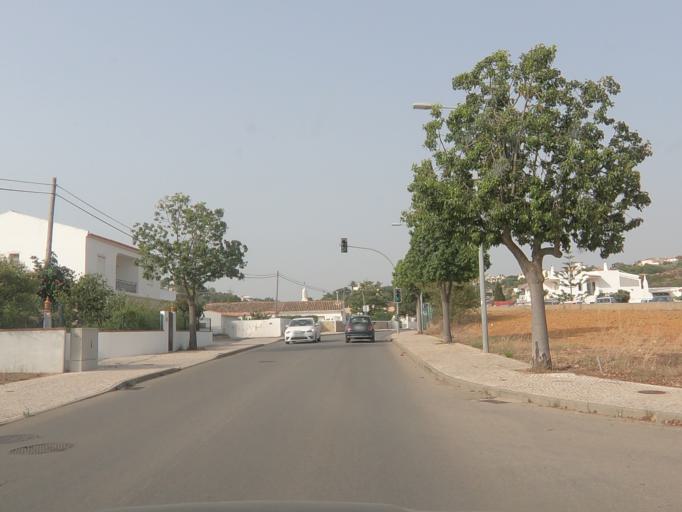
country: PT
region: Faro
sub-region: Albufeira
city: Guia
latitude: 37.0866
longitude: -8.2952
